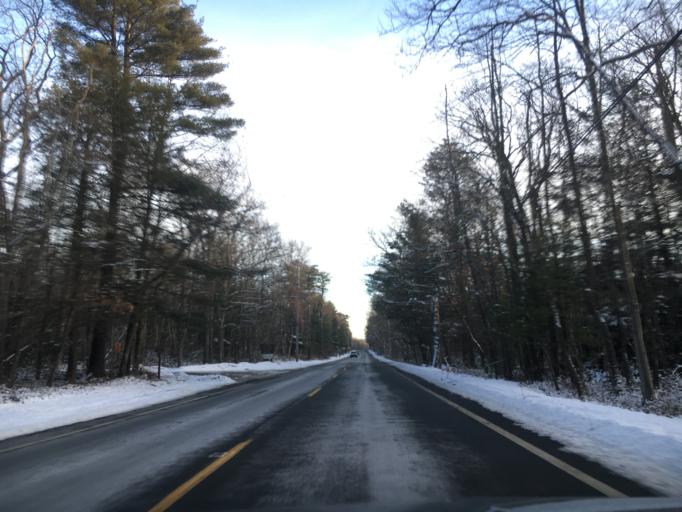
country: US
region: Pennsylvania
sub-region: Pike County
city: Hemlock Farms
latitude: 41.3045
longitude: -75.1021
